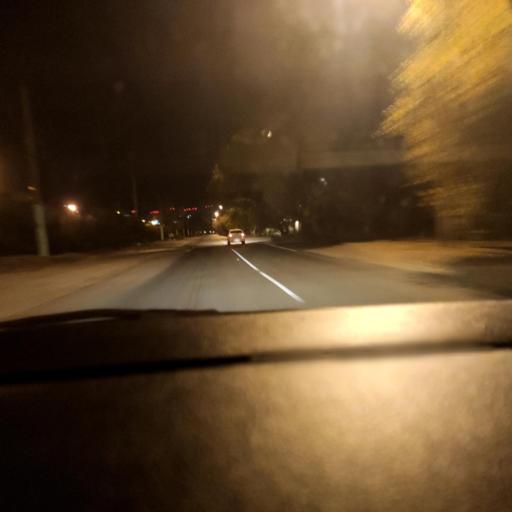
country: RU
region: Voronezj
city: Voronezh
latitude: 51.6969
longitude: 39.1553
